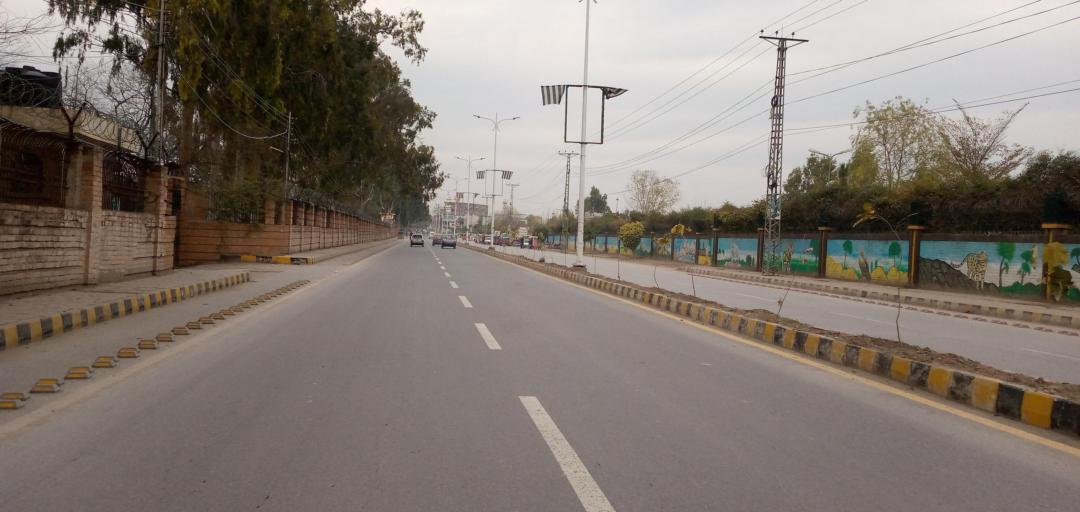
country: PK
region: Khyber Pakhtunkhwa
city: Peshawar
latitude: 34.0149
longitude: 71.4892
